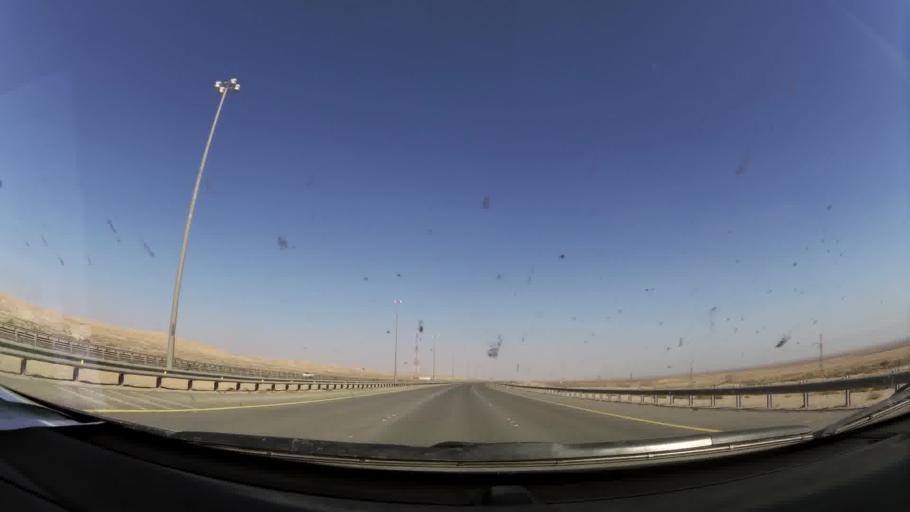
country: KW
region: Al Asimah
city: Kuwait City
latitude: 29.5296
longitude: 47.8250
